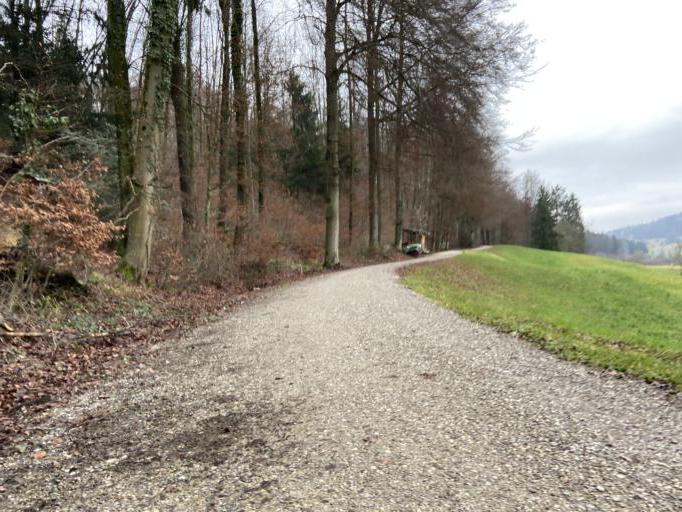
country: CH
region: Zurich
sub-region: Bezirk Winterthur
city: Toess (Kreis 4) / Vorder-Daettnau
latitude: 47.4821
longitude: 8.6901
